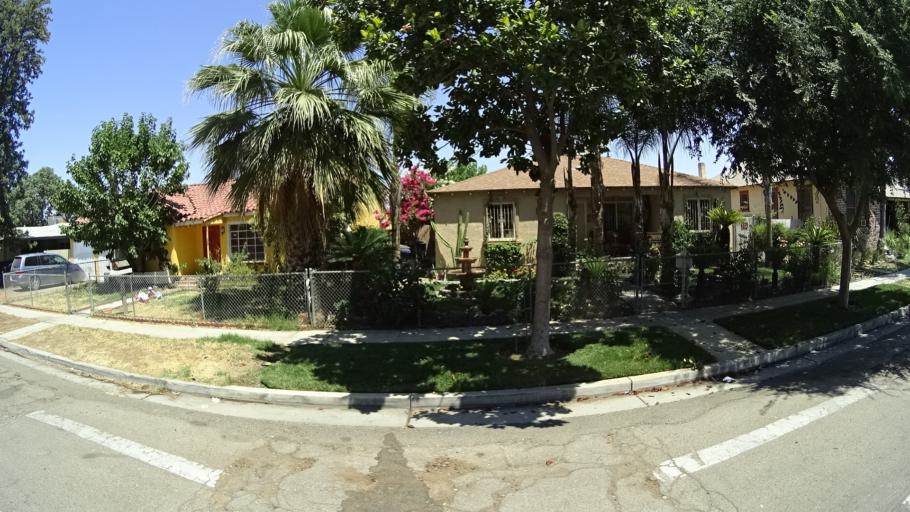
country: US
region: California
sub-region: Fresno County
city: West Park
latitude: 36.7274
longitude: -119.8146
